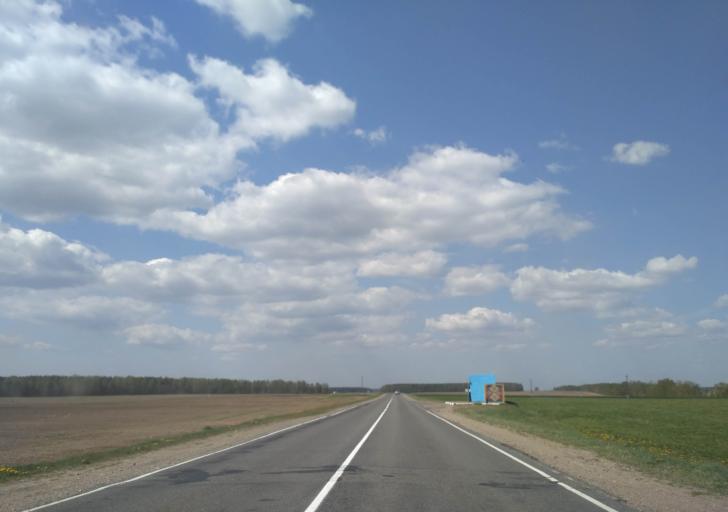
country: BY
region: Minsk
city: Vilyeyka
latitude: 54.5135
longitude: 27.0456
